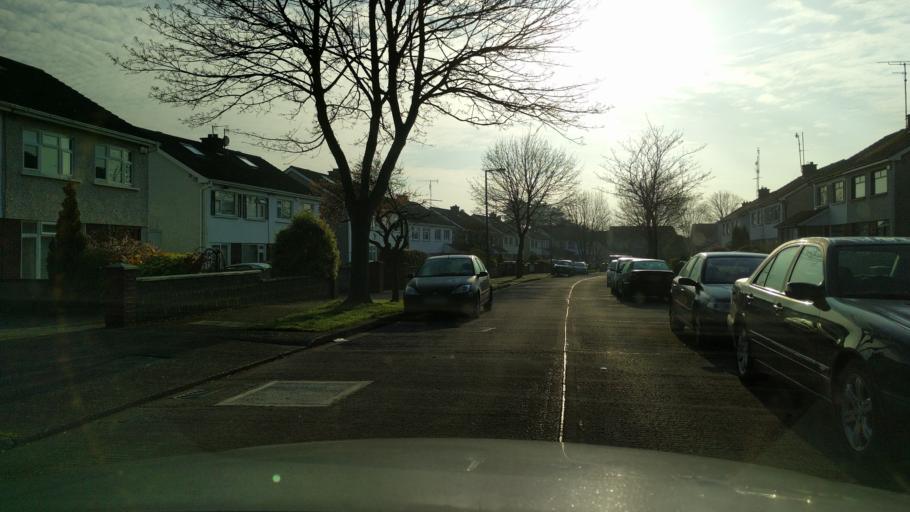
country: IE
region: Leinster
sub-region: Fingal County
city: Swords
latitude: 53.4534
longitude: -6.2321
